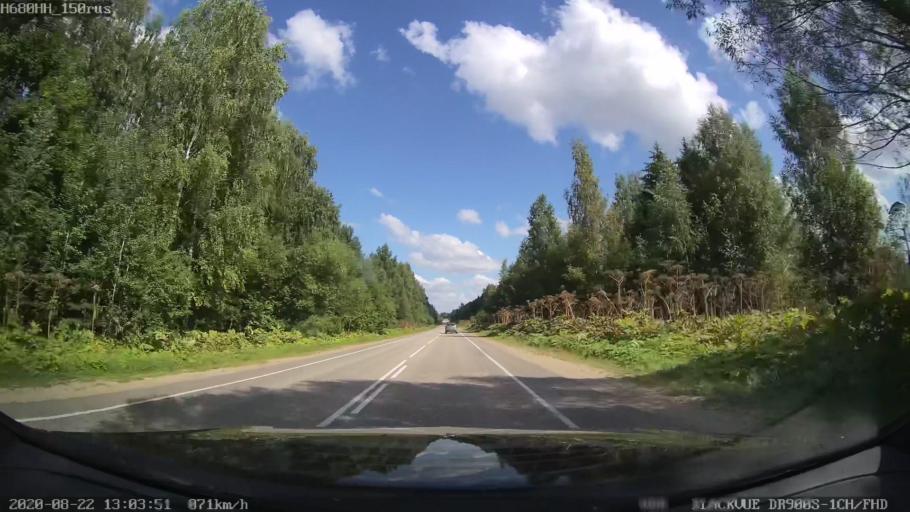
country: RU
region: Tverskaya
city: Bezhetsk
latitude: 57.6621
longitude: 36.4176
